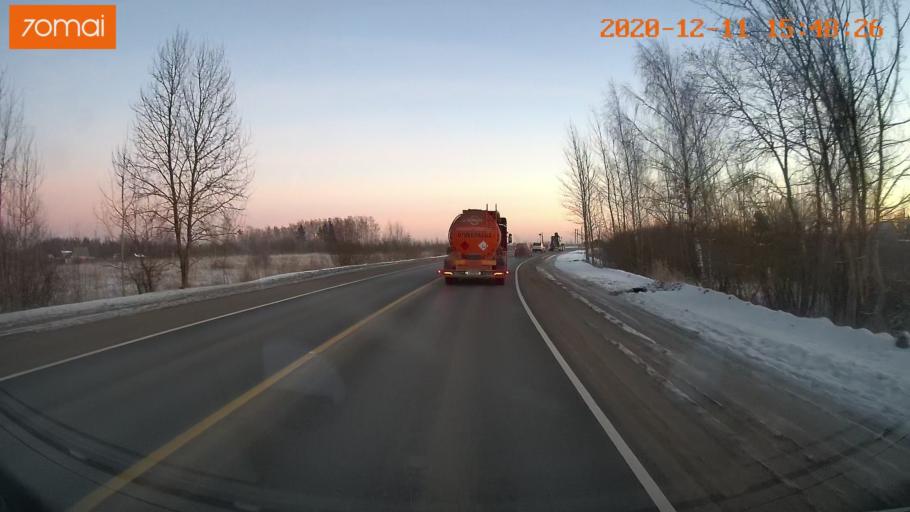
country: RU
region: Ivanovo
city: Novo-Talitsy
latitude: 56.9927
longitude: 40.8683
